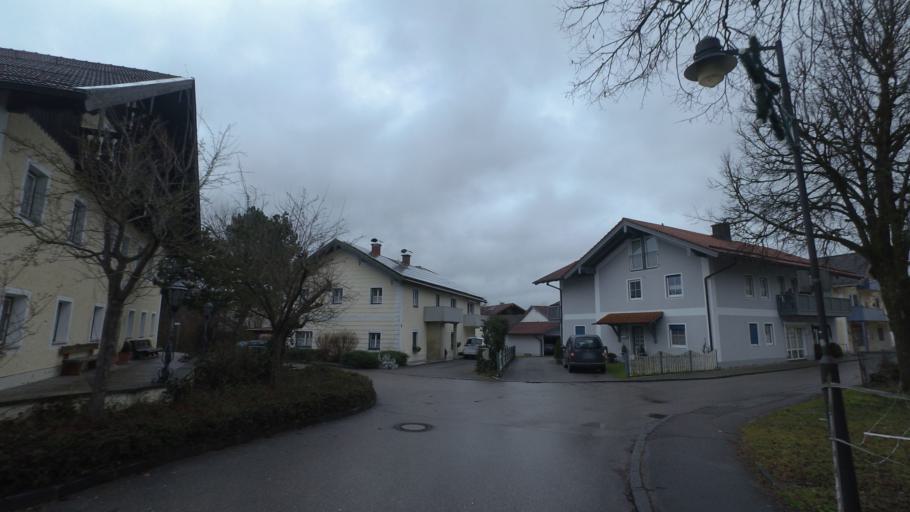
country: DE
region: Bavaria
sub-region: Upper Bavaria
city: Kirchanschoring
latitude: 47.9536
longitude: 12.8348
